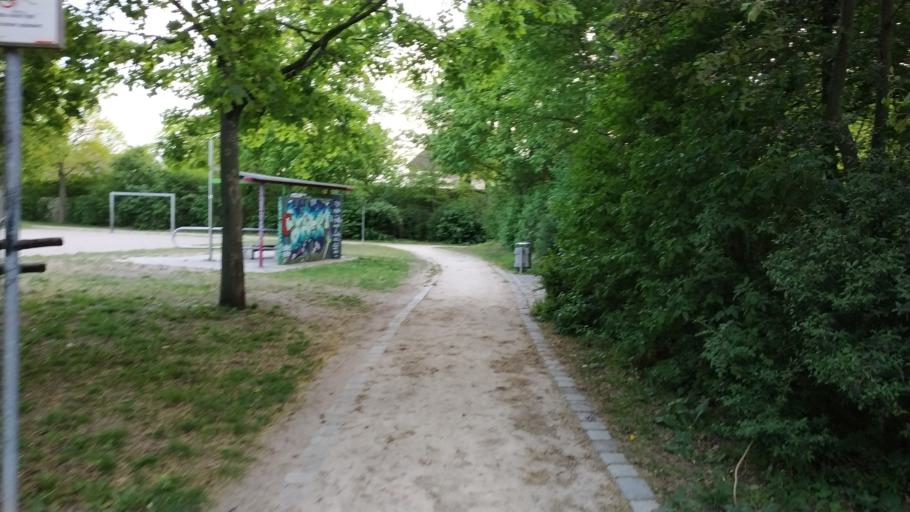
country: DE
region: Bavaria
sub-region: Regierungsbezirk Mittelfranken
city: Nuernberg
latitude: 49.4683
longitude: 11.0624
